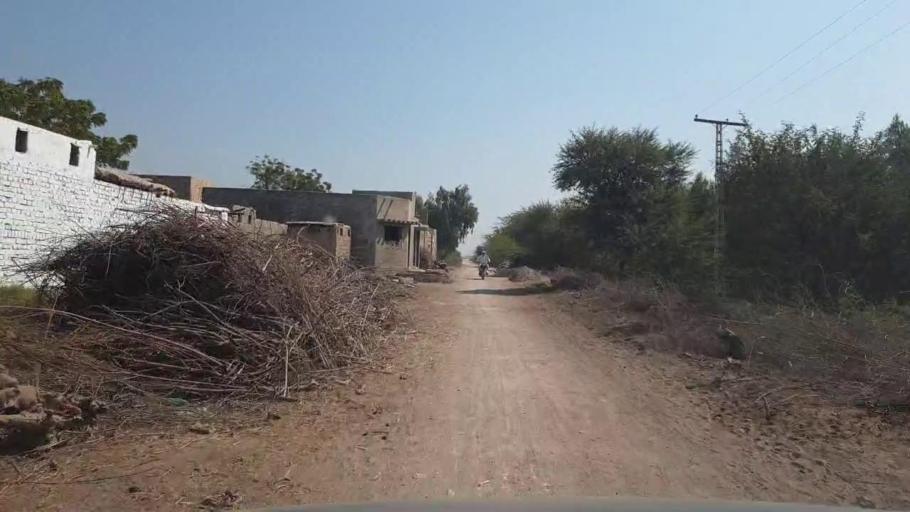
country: PK
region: Sindh
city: Digri
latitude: 25.2098
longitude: 69.1950
